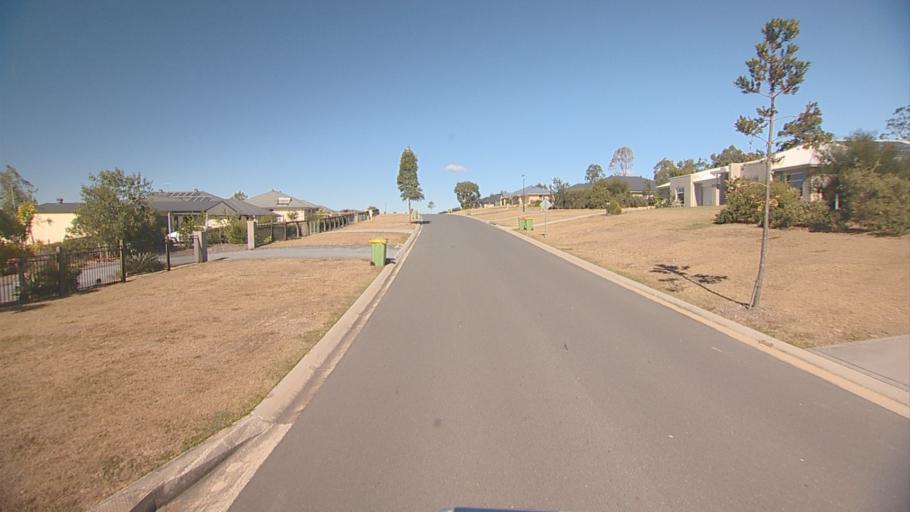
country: AU
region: Queensland
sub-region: Logan
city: North Maclean
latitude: -27.7542
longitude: 152.9446
